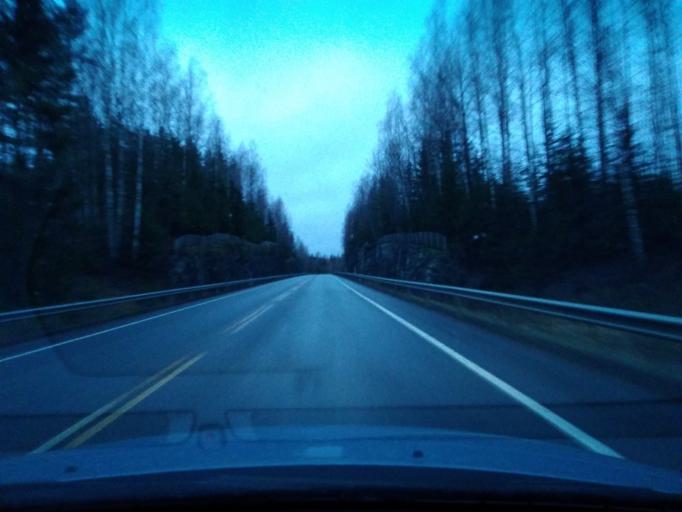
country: FI
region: Uusimaa
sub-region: Porvoo
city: Porvoo
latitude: 60.4053
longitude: 25.5890
